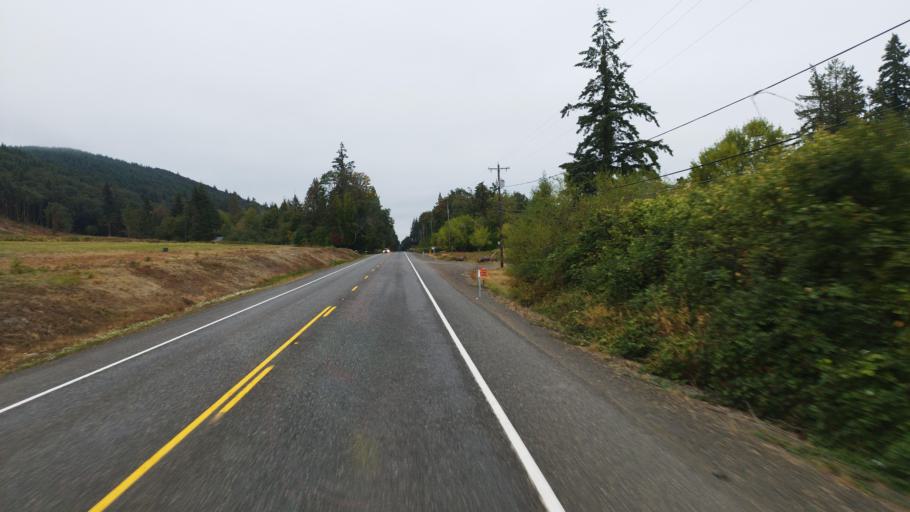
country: US
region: Oregon
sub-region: Columbia County
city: Rainier
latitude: 46.0671
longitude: -122.8987
